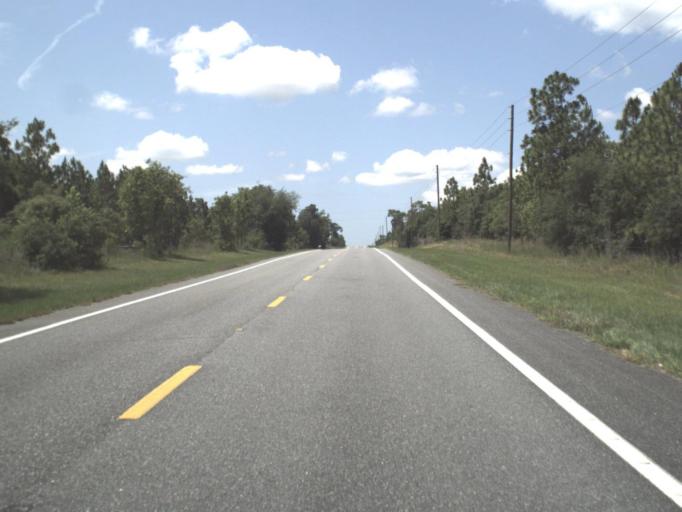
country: US
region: Florida
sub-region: Levy County
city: Williston Highlands
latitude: 29.2391
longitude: -82.5580
